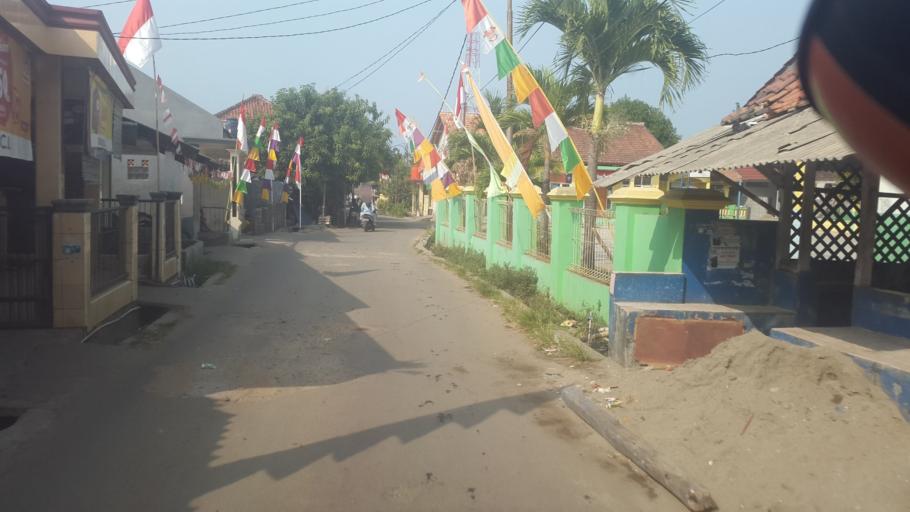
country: ID
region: West Java
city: Tugu
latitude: -6.9499
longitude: 106.4442
